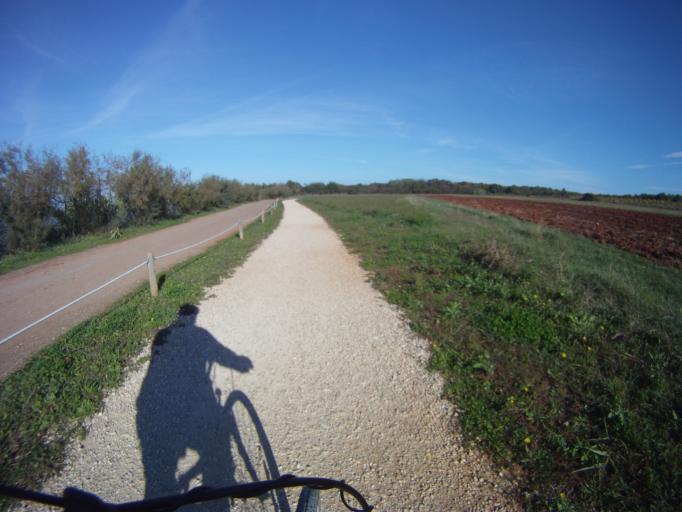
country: HR
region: Istarska
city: Novigrad
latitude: 45.3335
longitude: 13.5444
